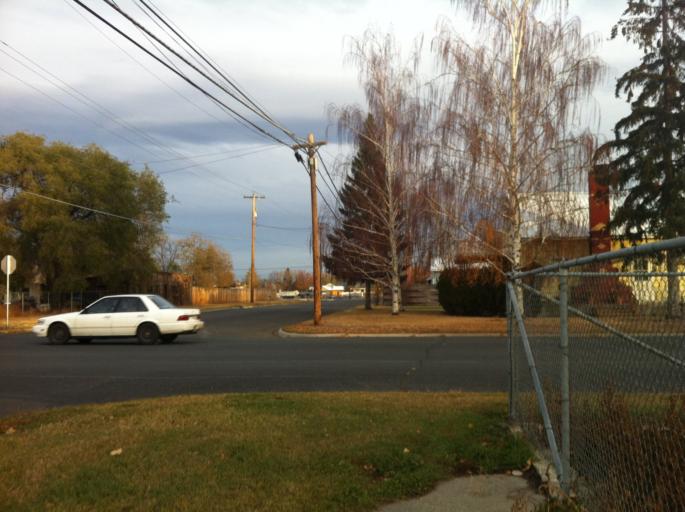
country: US
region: Oregon
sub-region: Baker County
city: Baker City
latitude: 44.7852
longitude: -117.8397
